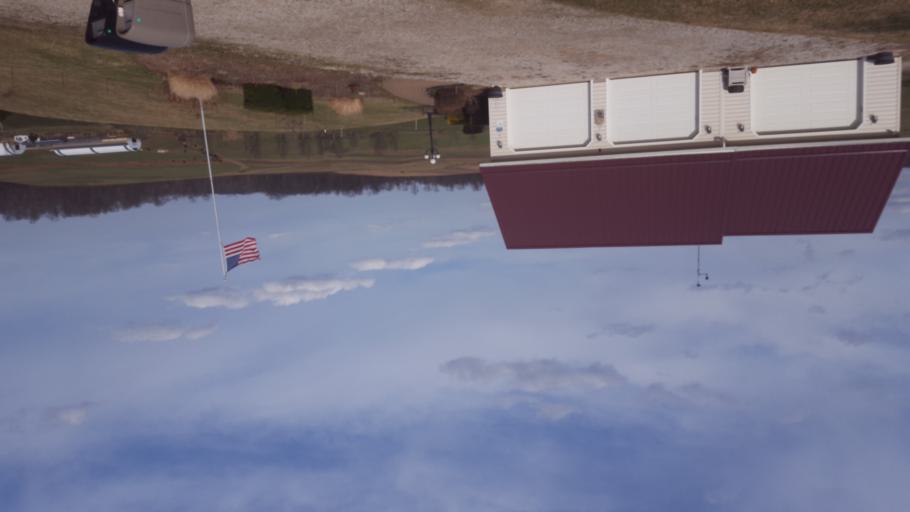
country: US
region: Ohio
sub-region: Knox County
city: Danville
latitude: 40.5460
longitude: -82.3418
